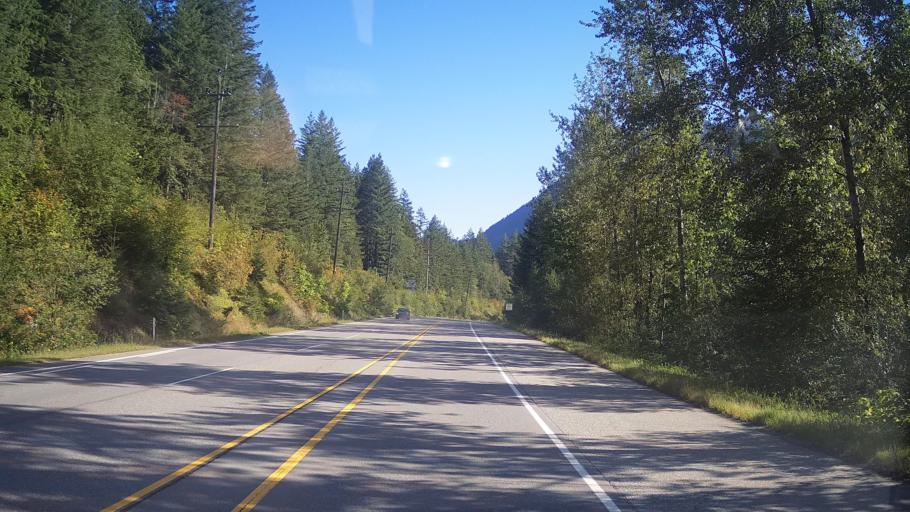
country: CA
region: British Columbia
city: Hope
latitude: 49.5026
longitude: -121.4196
